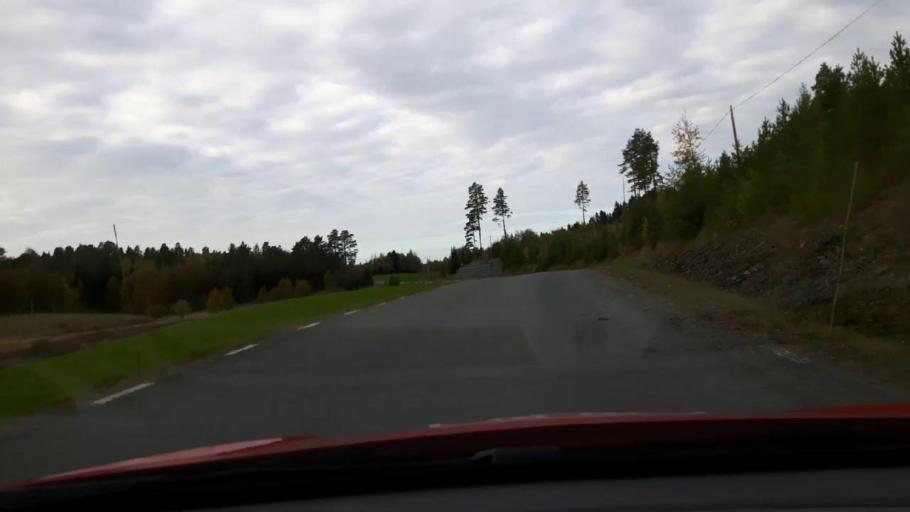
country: SE
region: Jaemtland
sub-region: Krokoms Kommun
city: Krokom
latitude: 63.2005
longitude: 14.1234
